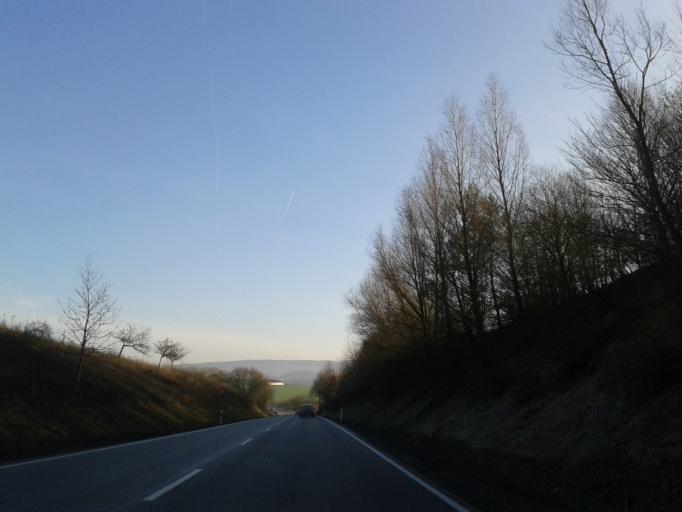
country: DE
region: Bavaria
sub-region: Regierungsbezirk Unterfranken
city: Hofheim in Unterfranken
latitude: 50.1241
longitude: 10.5015
